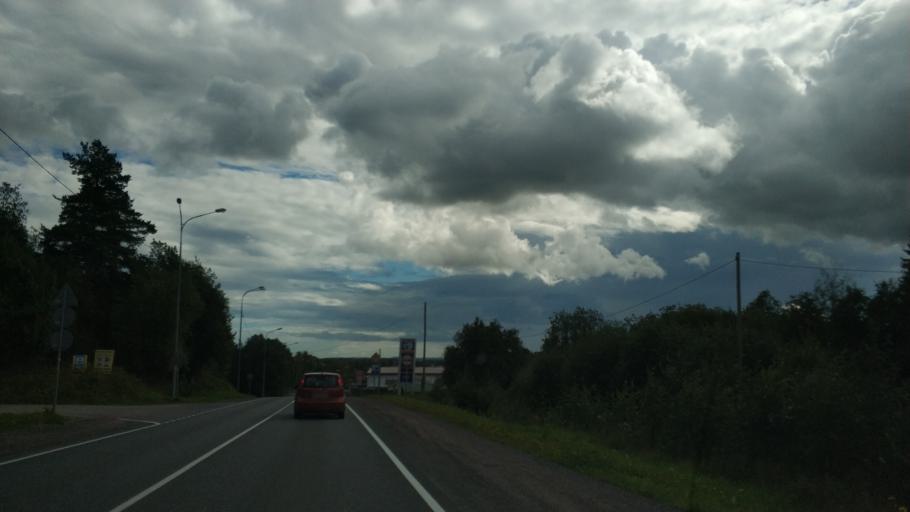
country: RU
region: Republic of Karelia
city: Khelyulya
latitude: 61.7543
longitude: 30.6578
